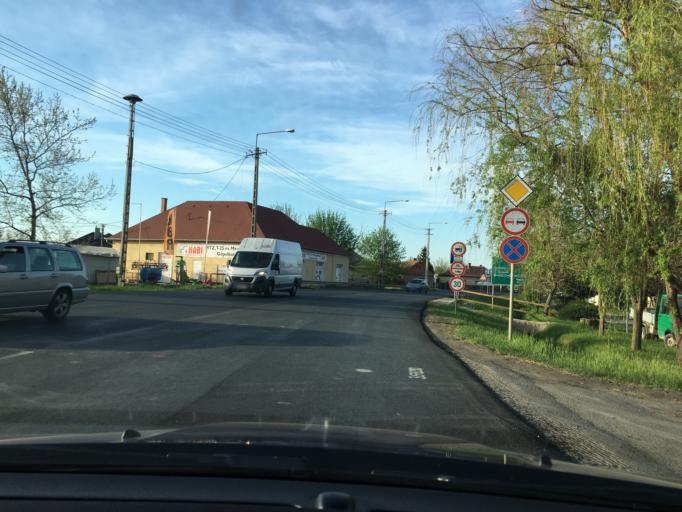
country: HU
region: Hajdu-Bihar
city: Berettyoujfalu
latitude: 47.2313
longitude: 21.5322
